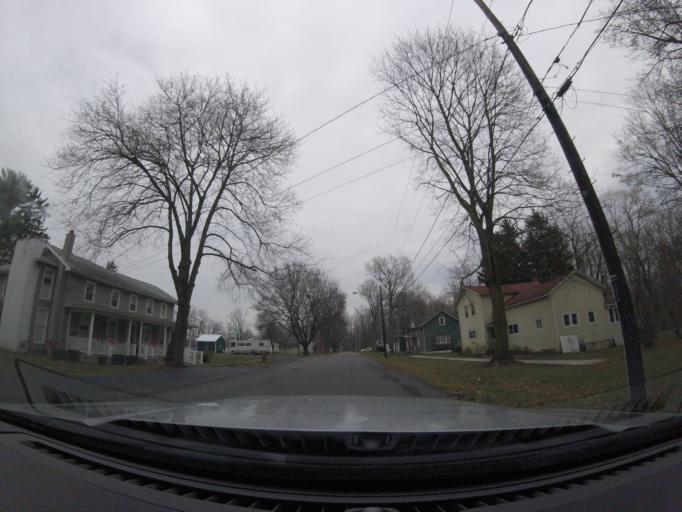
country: US
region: New York
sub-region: Yates County
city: Penn Yan
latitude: 42.6828
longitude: -76.9535
